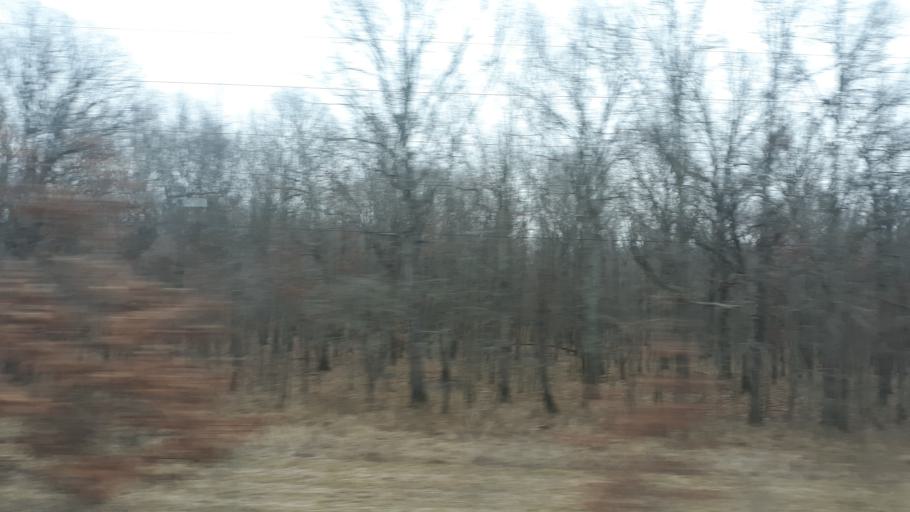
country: US
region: Illinois
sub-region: Saline County
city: Eldorado
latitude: 37.8864
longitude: -88.3864
